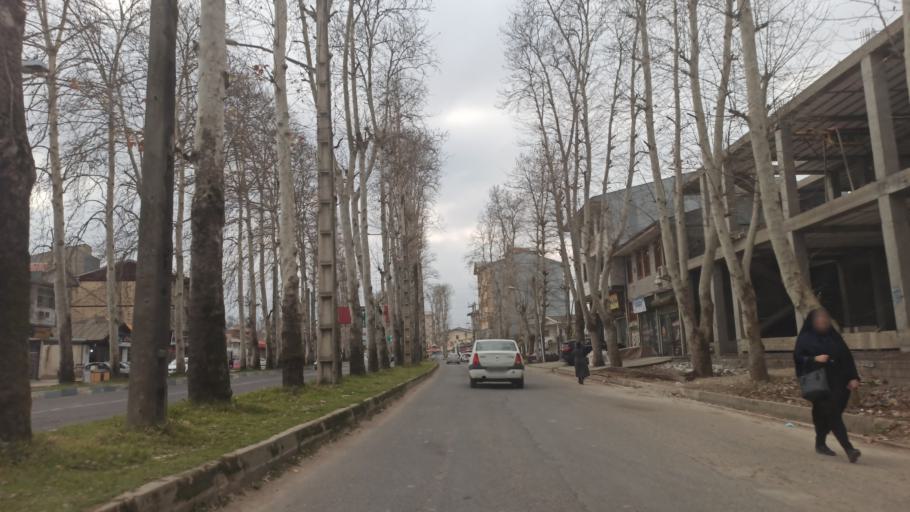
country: IR
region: Gilan
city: Fuman
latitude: 37.2344
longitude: 49.3217
